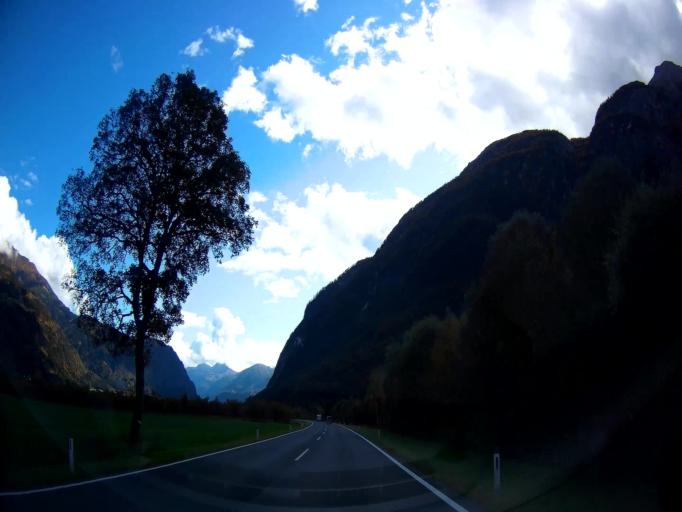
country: AT
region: Tyrol
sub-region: Politischer Bezirk Lienz
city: Nikolsdorf
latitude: 46.7873
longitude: 12.8792
